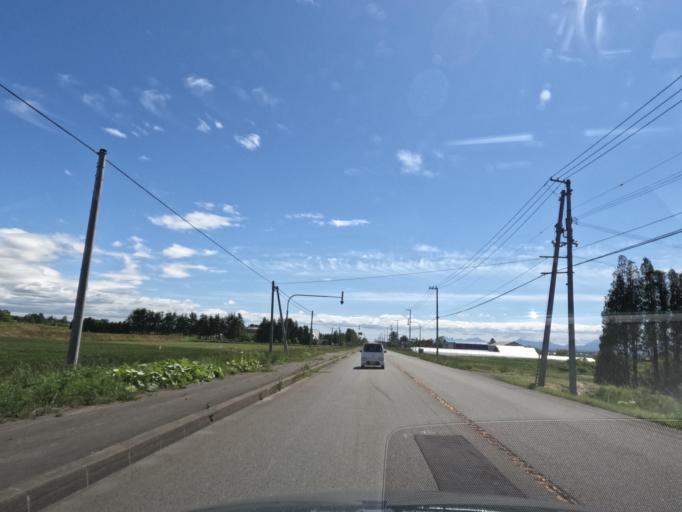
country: JP
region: Hokkaido
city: Kitahiroshima
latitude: 43.0393
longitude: 141.7203
